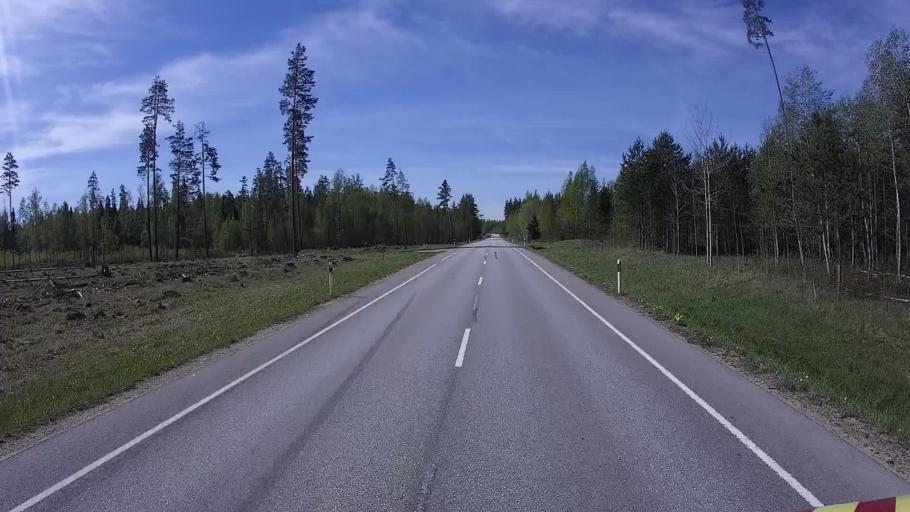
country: RU
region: Pskov
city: Pechory
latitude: 57.9141
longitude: 27.5591
